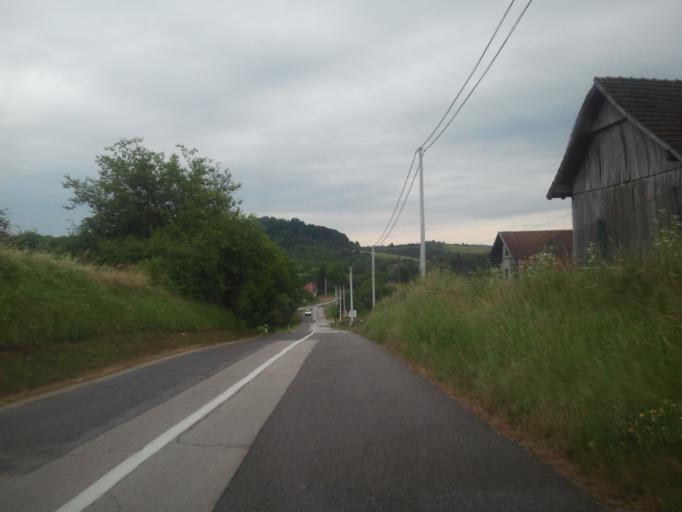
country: HR
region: Karlovacka
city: Vojnic
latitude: 45.3424
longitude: 15.6861
